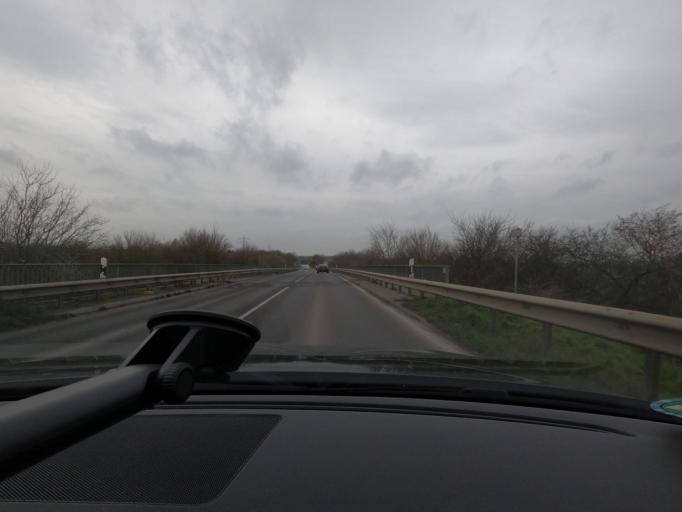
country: DE
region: North Rhine-Westphalia
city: Kempen
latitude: 51.3798
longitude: 6.4183
